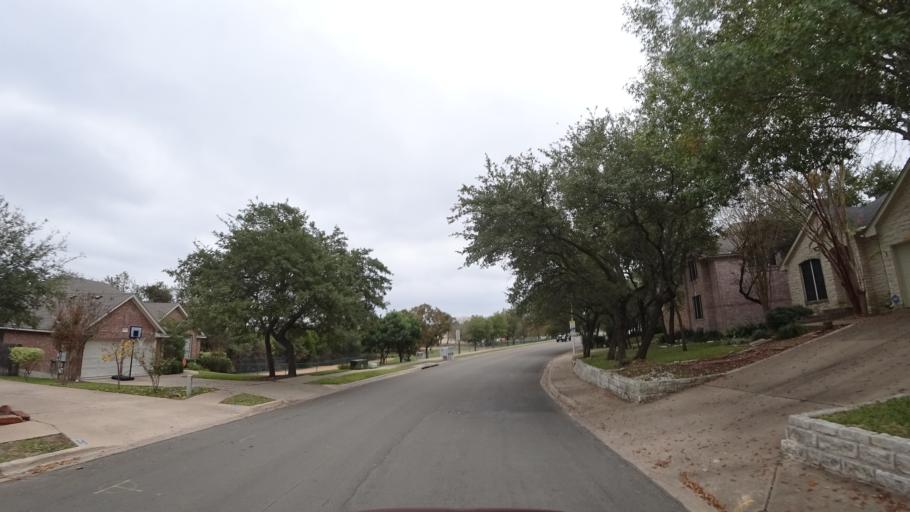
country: US
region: Texas
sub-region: Williamson County
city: Anderson Mill
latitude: 30.4381
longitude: -97.8263
